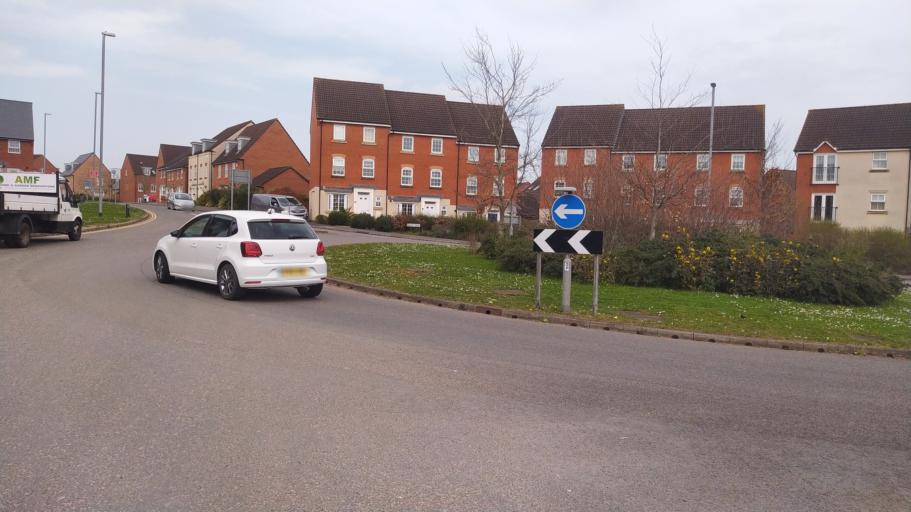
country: GB
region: England
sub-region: Somerset
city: Taunton
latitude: 51.0281
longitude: -3.1368
